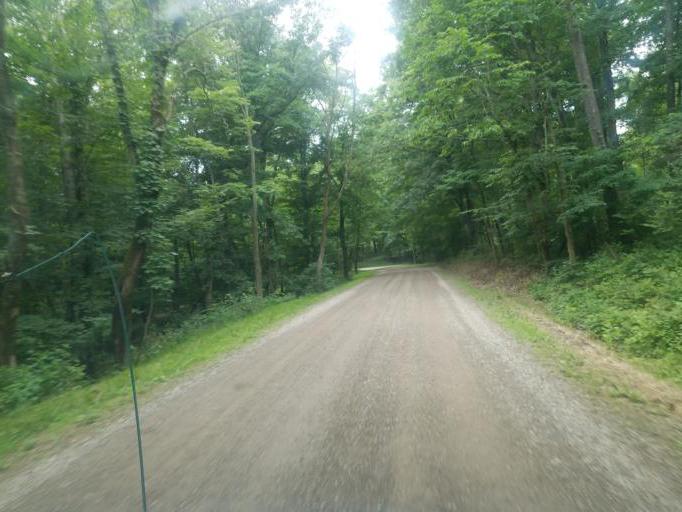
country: US
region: Ohio
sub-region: Knox County
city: Oak Hill
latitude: 40.4326
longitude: -82.1504
